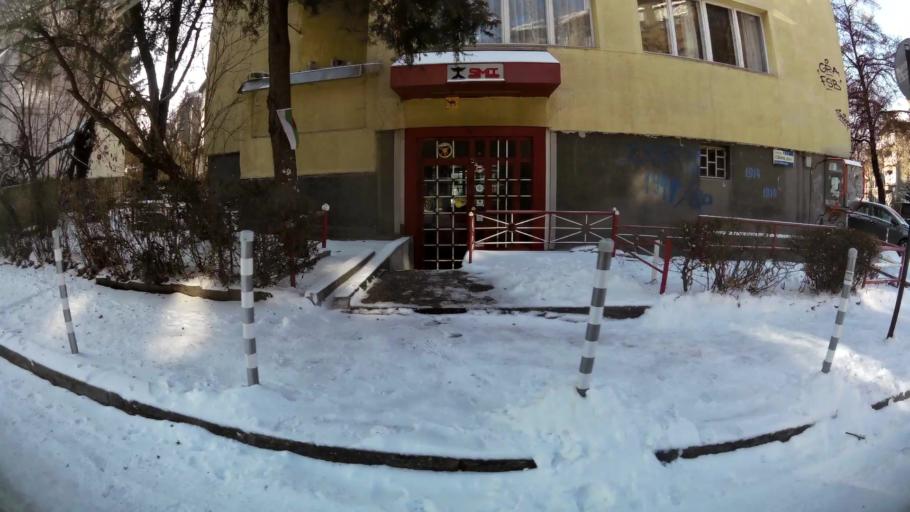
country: BG
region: Sofia-Capital
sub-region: Stolichna Obshtina
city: Sofia
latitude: 42.6805
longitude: 23.3282
